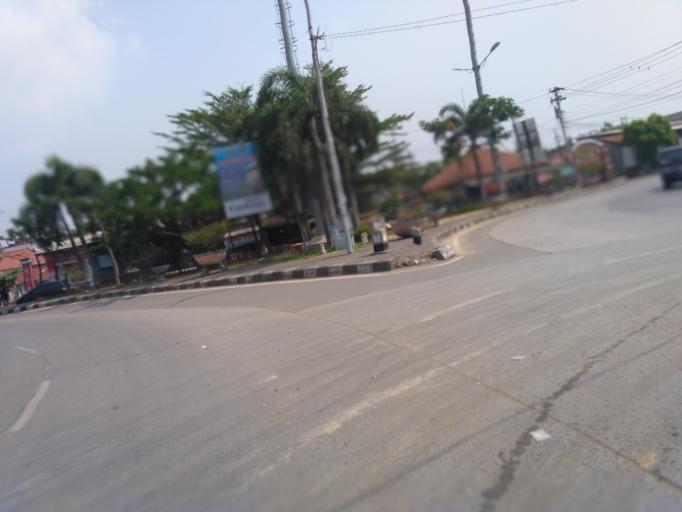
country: ID
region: Central Java
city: Semarang
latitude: -6.9608
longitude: 110.4400
